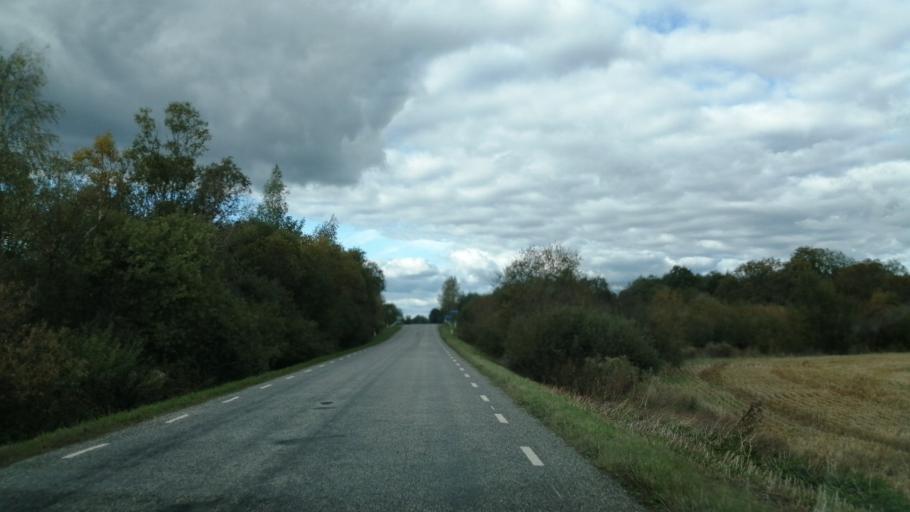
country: EE
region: Jaervamaa
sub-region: Tueri vald
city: Tueri
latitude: 58.7982
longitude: 25.4780
